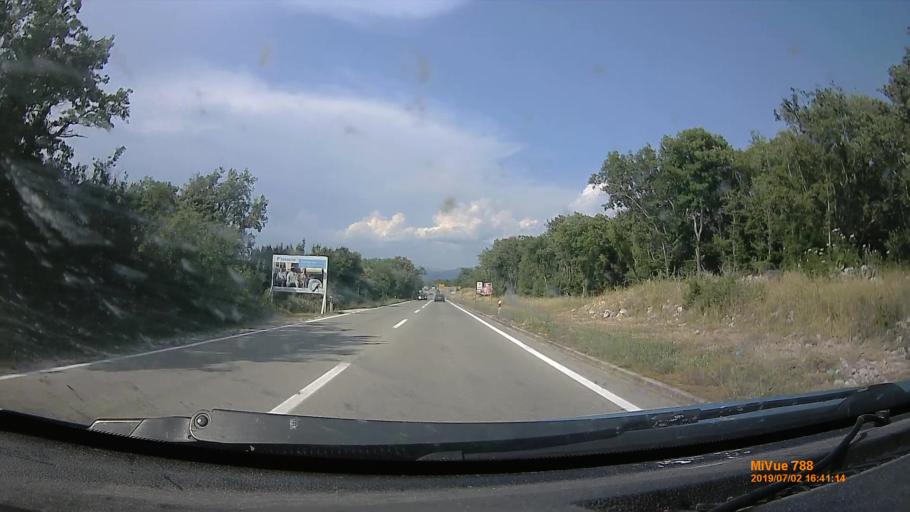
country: HR
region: Primorsko-Goranska
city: Njivice
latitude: 45.1161
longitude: 14.5477
